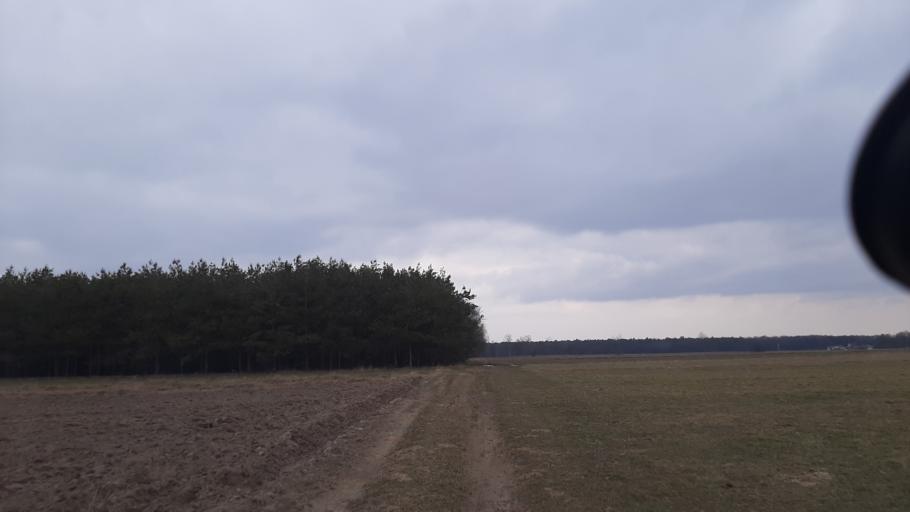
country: PL
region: Lublin Voivodeship
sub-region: Powiat lubelski
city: Garbow
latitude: 51.3843
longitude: 22.4074
